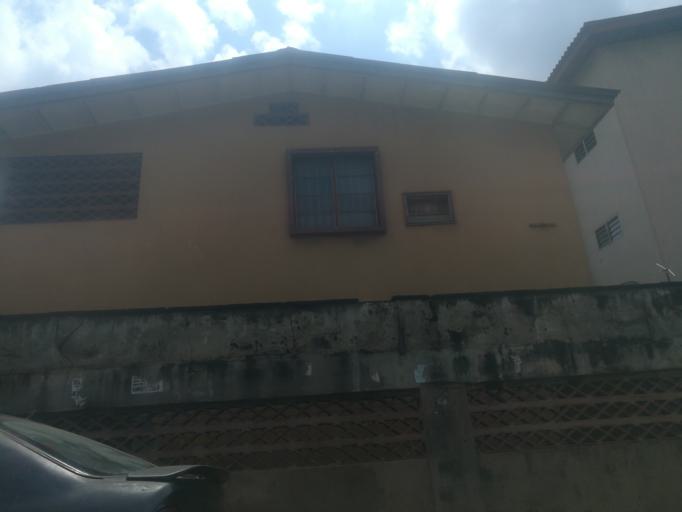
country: NG
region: Lagos
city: Ojota
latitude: 6.5970
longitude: 3.3902
